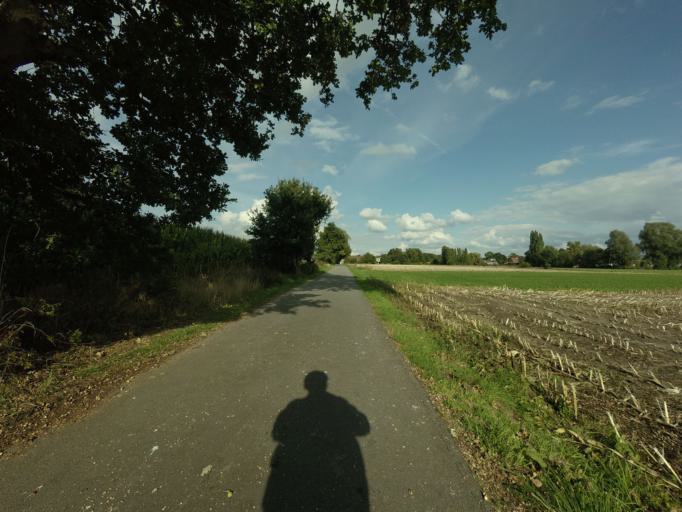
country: BE
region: Flanders
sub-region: Provincie Antwerpen
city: Boom
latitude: 51.1061
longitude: 4.3810
